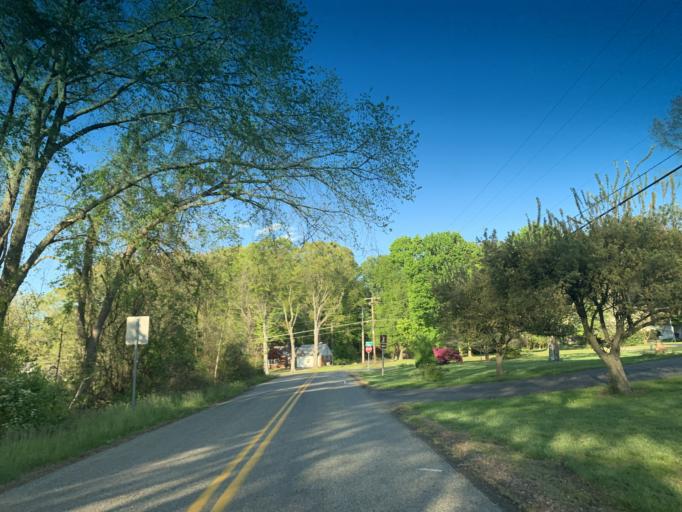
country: US
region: Maryland
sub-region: Harford County
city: Aberdeen
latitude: 39.5406
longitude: -76.1798
